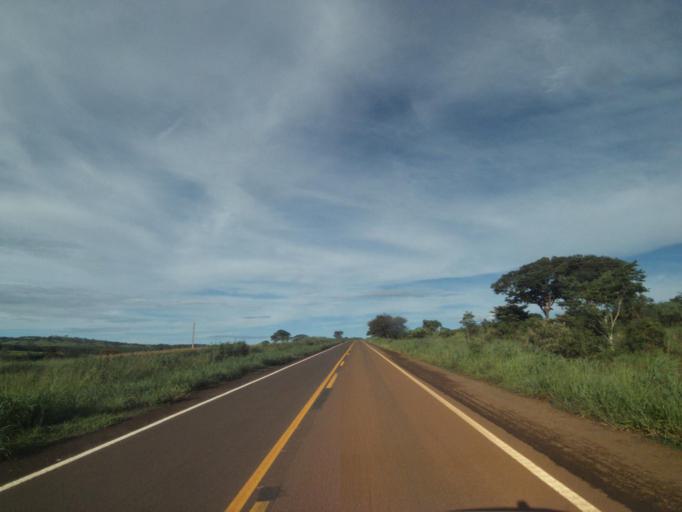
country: BR
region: Goias
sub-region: Jaragua
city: Jaragua
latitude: -15.9082
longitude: -49.5568
